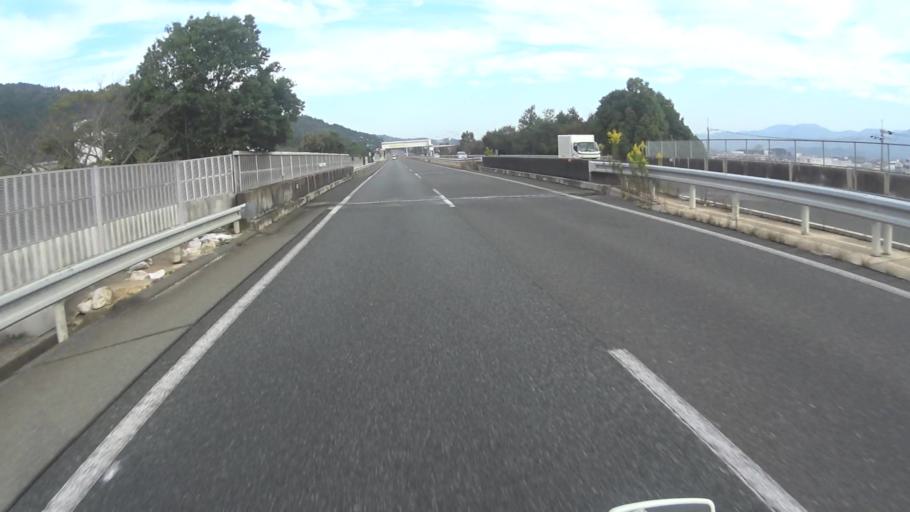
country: JP
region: Kyoto
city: Kameoka
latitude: 35.0305
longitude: 135.5453
